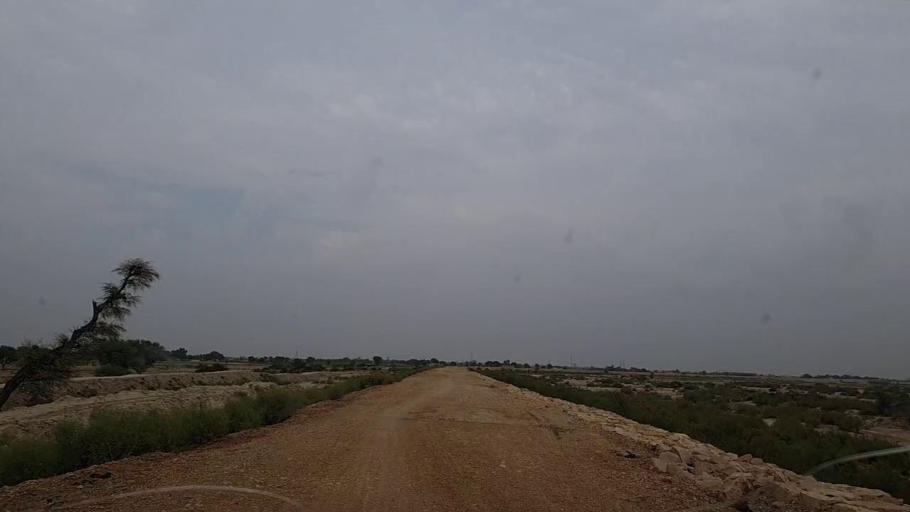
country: PK
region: Sindh
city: Johi
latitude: 26.7056
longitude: 67.5916
